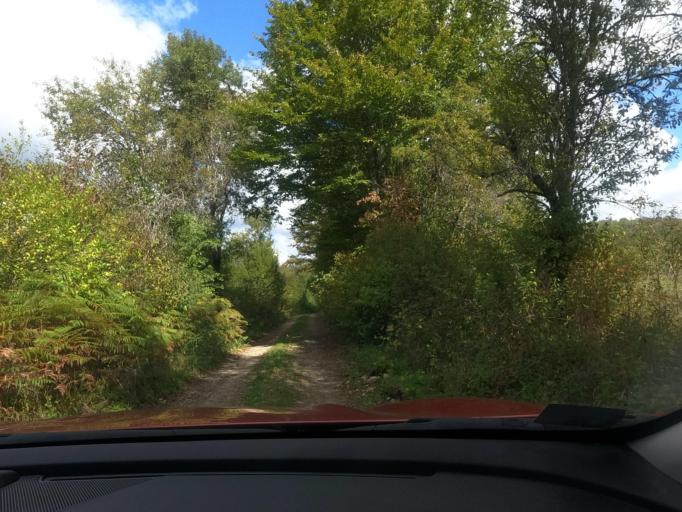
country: BA
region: Federation of Bosnia and Herzegovina
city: Velika Kladusa
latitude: 45.2324
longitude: 15.7739
